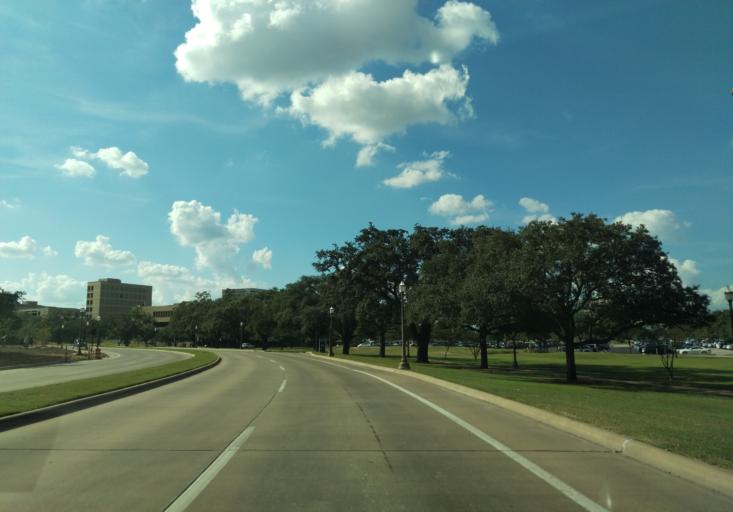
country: US
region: Texas
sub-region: Brazos County
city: College Station
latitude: 30.6203
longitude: -96.3360
